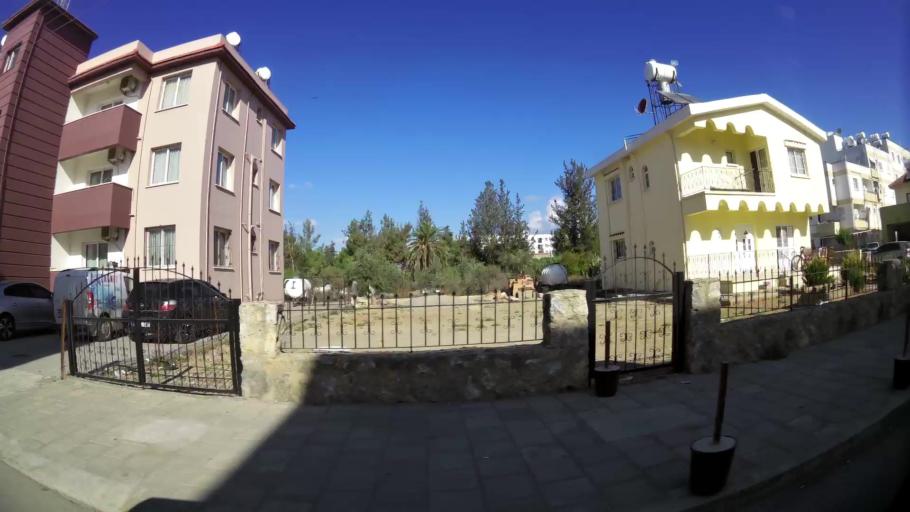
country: CY
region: Lefkosia
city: Nicosia
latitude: 35.2120
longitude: 33.3096
